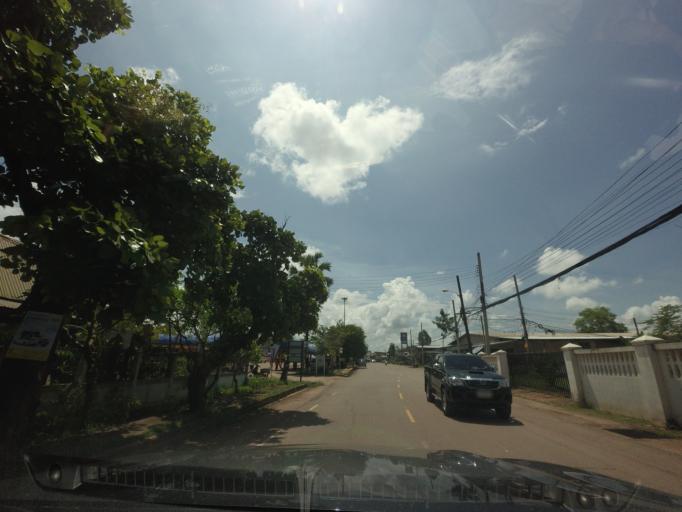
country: TH
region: Changwat Udon Thani
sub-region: Amphoe Ban Phue
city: Ban Phue
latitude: 17.6928
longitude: 102.4663
